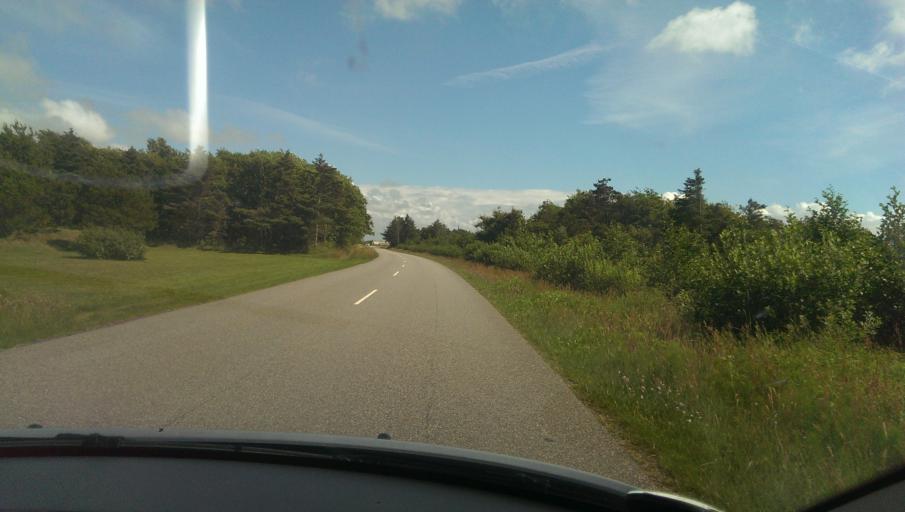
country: DK
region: Central Jutland
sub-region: Ringkobing-Skjern Kommune
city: Ringkobing
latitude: 56.1407
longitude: 8.1496
